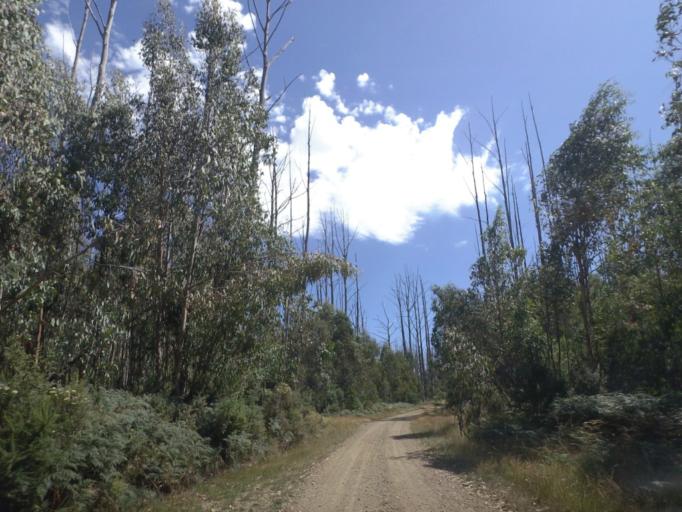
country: AU
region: Victoria
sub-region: Murrindindi
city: Alexandra
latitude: -37.4743
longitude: 145.8376
